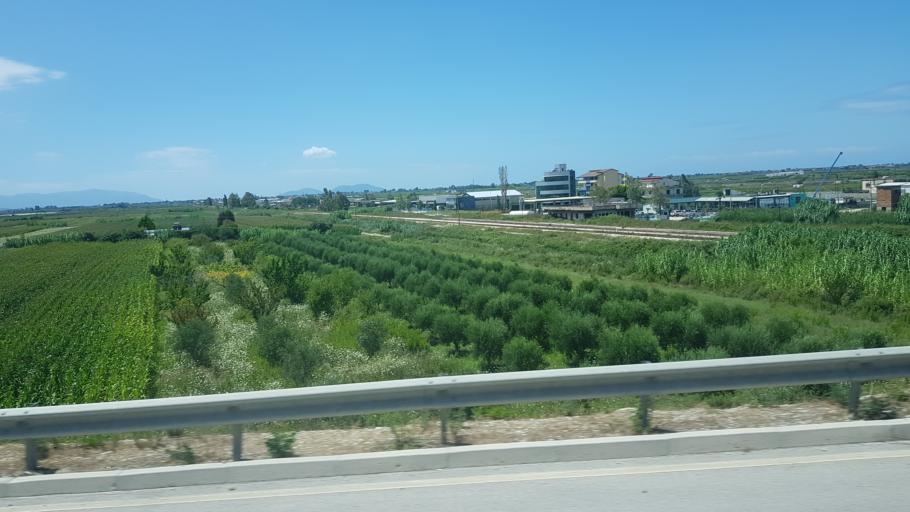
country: AL
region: Fier
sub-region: Rrethi i Fierit
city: Levan
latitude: 40.6686
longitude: 19.4856
